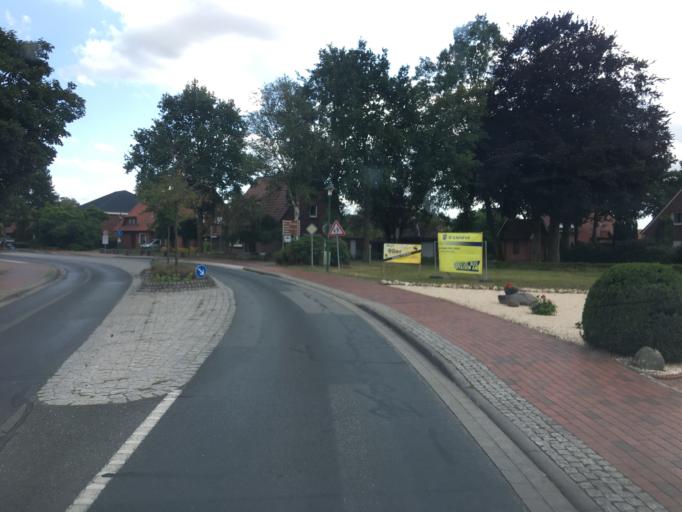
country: DE
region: Lower Saxony
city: Hilkenbrook
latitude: 53.0700
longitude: 7.7033
